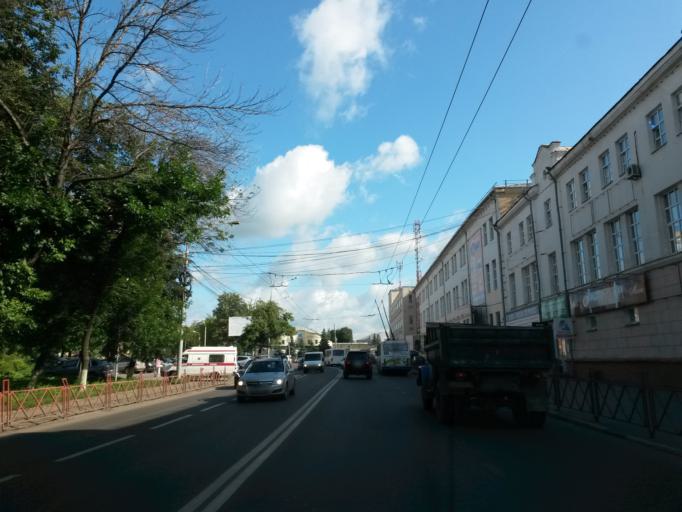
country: RU
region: Jaroslavl
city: Yaroslavl
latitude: 57.6401
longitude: 39.8833
